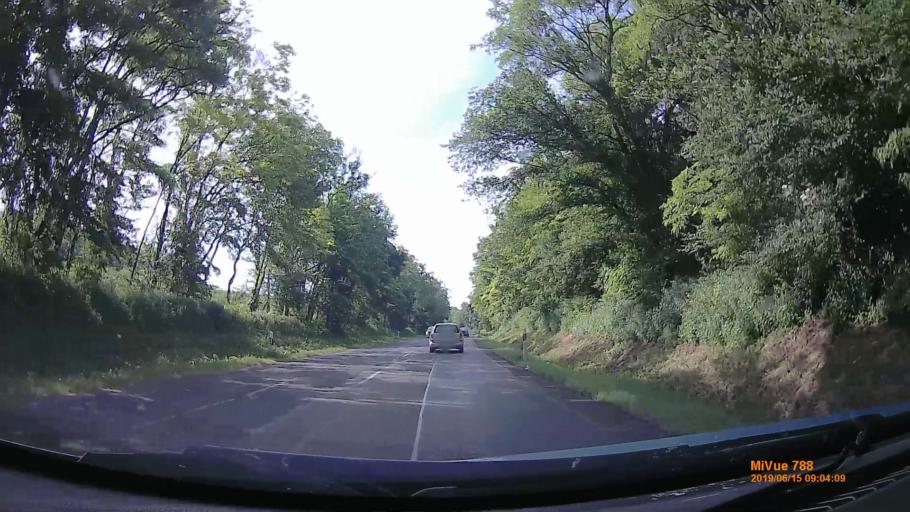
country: HU
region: Tolna
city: Iregszemcse
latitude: 46.7393
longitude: 18.1634
